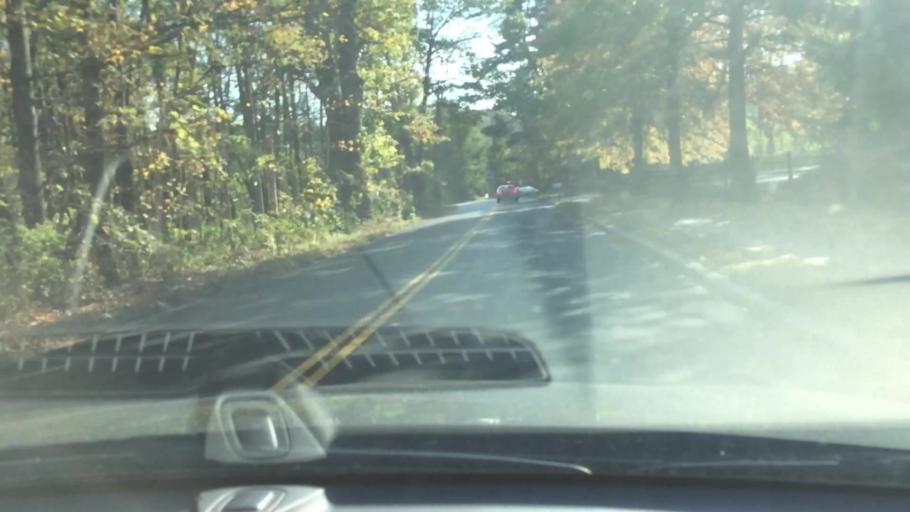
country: US
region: New York
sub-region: Saratoga County
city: Saratoga Springs
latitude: 43.0919
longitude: -73.7626
